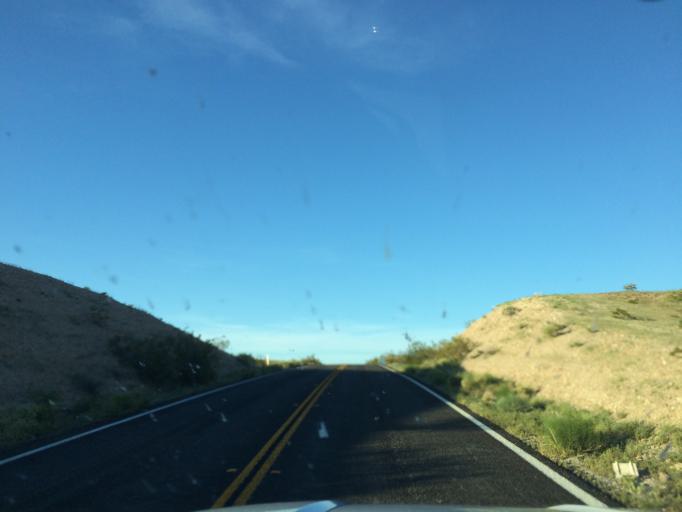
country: US
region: California
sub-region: Riverside County
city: Mesa Verde
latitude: 33.2004
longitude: -114.8577
